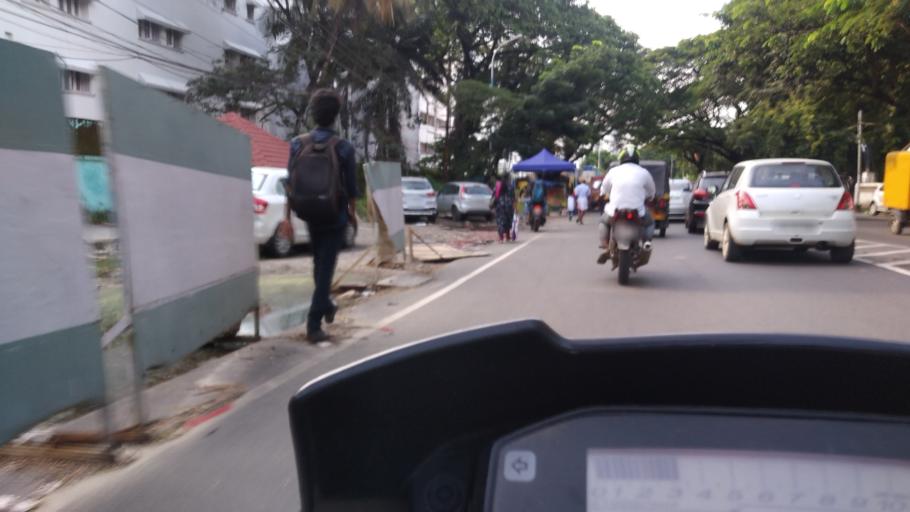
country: IN
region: Kerala
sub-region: Ernakulam
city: Cochin
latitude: 9.9856
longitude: 76.2730
